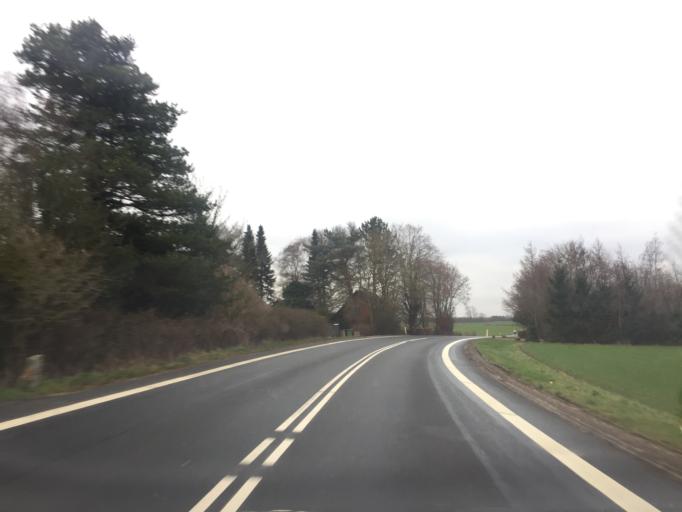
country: DK
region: South Denmark
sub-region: Svendborg Kommune
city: Thuro By
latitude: 55.1392
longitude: 10.6736
